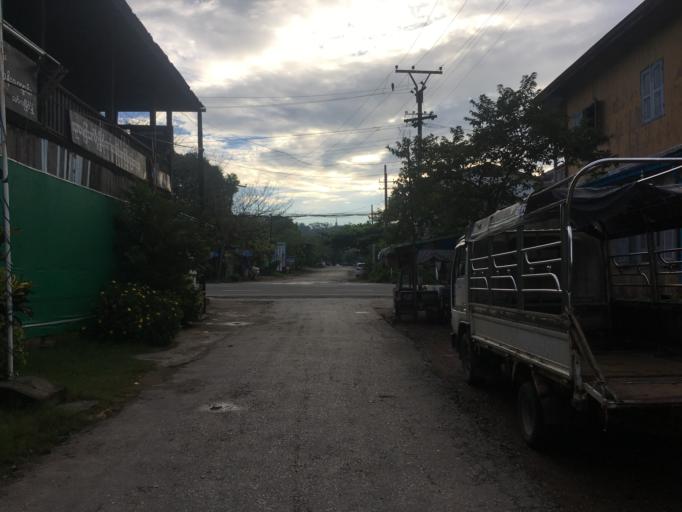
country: MM
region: Mon
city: Mawlamyine
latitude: 16.4768
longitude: 97.6202
